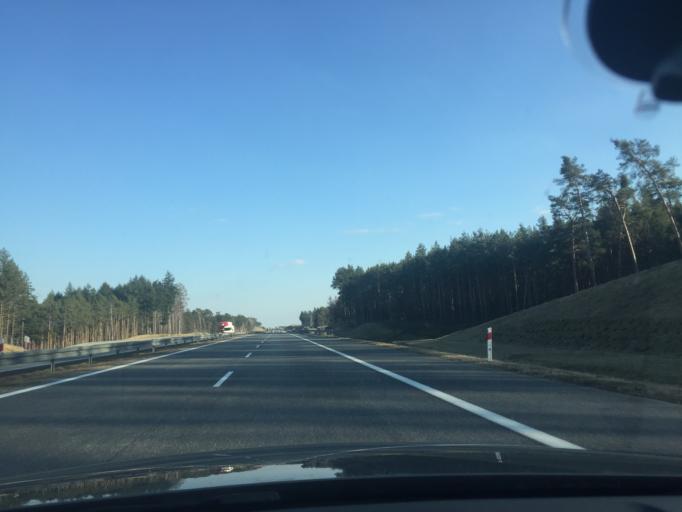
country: PL
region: Lubusz
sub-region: Powiat miedzyrzecki
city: Brojce
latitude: 52.3100
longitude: 15.6167
